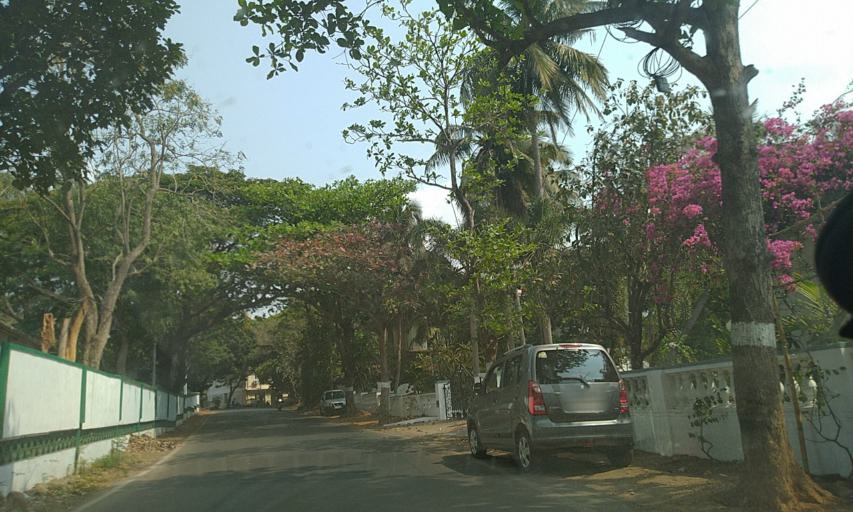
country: IN
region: Goa
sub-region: North Goa
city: Panaji
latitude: 15.4904
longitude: 73.8273
